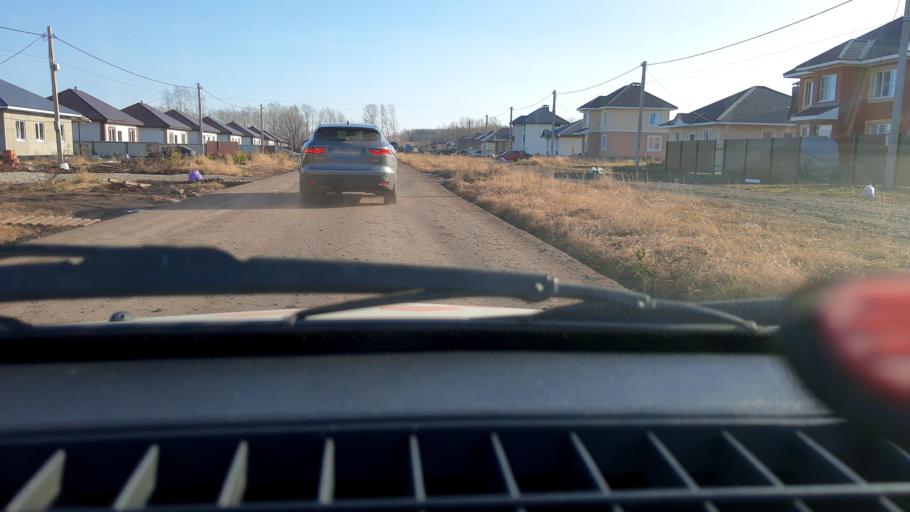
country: RU
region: Bashkortostan
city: Kabakovo
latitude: 54.6256
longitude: 56.1371
